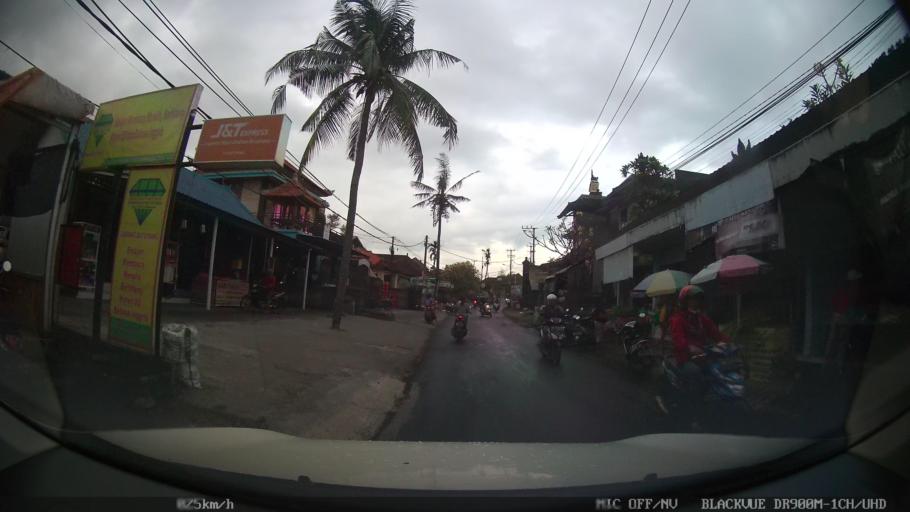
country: ID
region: Bali
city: Banjar Pasekan
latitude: -8.6255
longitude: 115.2715
